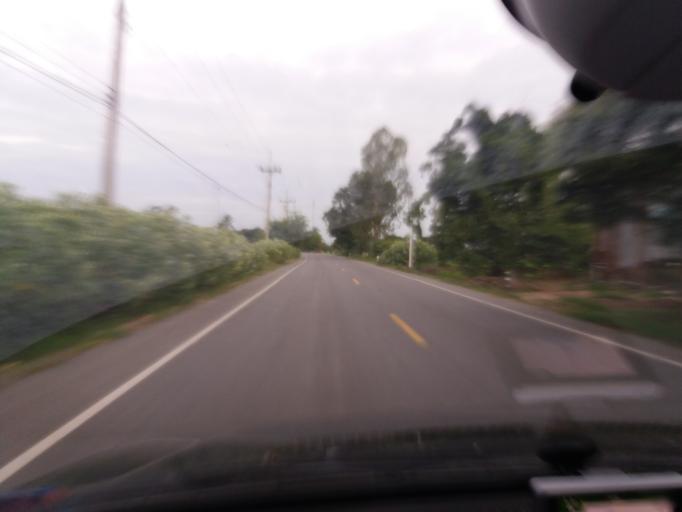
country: TH
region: Suphan Buri
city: Ban Sam Chuk
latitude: 14.7072
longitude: 100.0329
